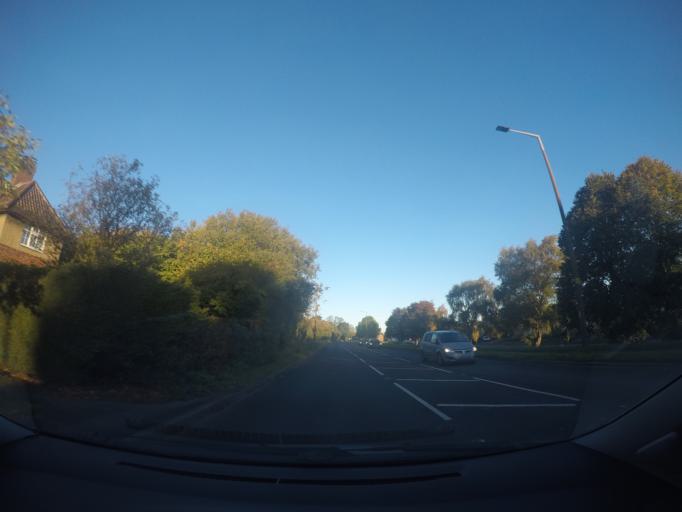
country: GB
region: England
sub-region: City of York
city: Skelton
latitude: 53.9812
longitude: -1.1161
